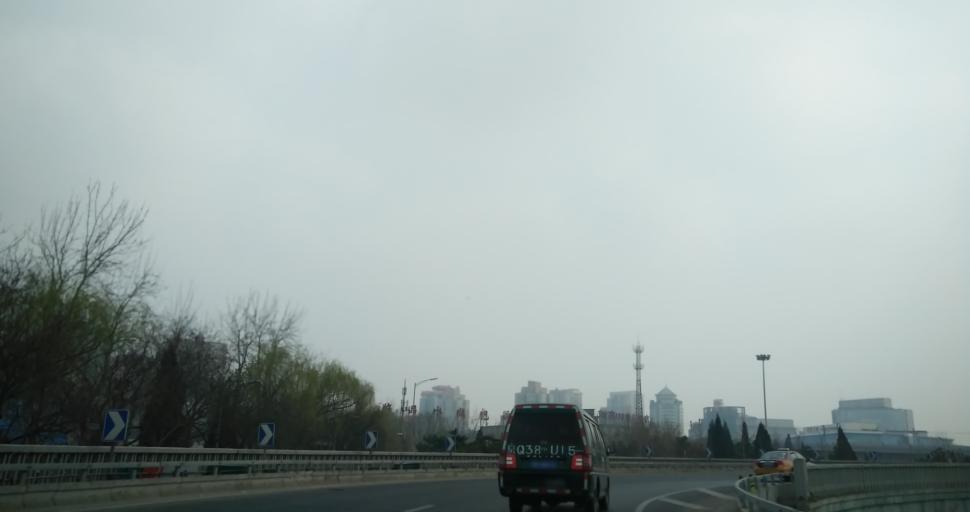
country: CN
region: Beijing
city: Longtan
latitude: 39.8616
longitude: 116.4470
